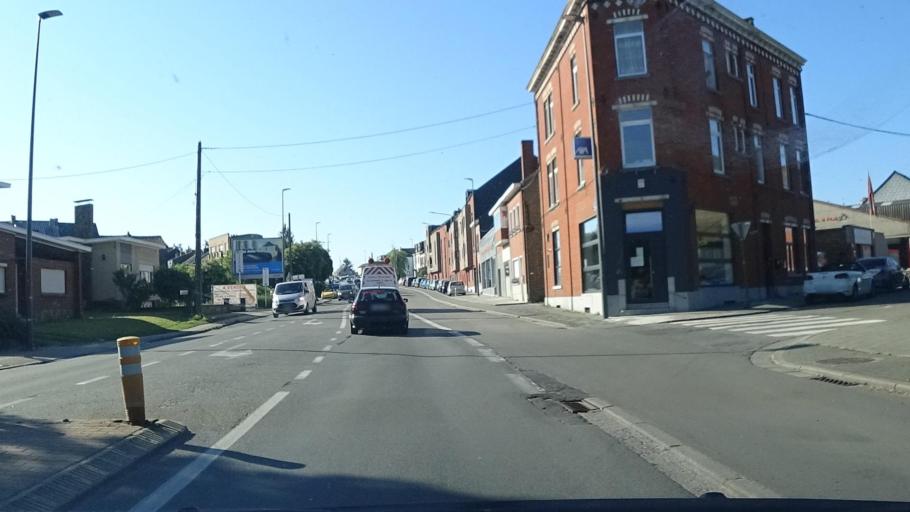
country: BE
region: Wallonia
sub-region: Province du Hainaut
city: La Louviere
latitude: 50.4740
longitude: 4.1817
